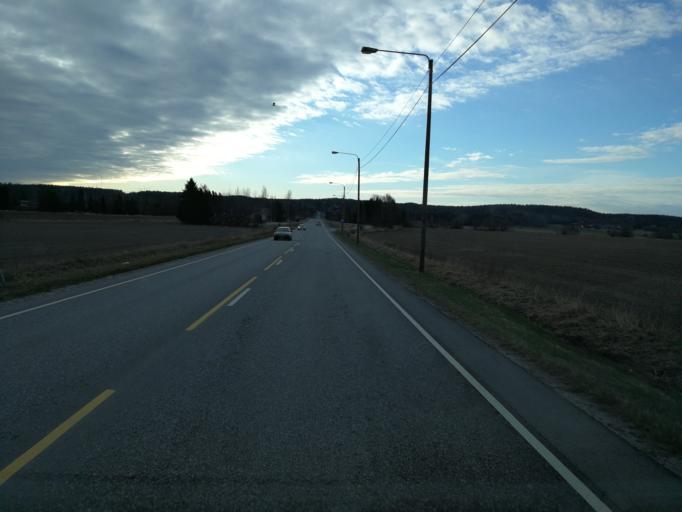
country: FI
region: Varsinais-Suomi
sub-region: Turku
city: Paimio
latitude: 60.4227
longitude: 22.6472
